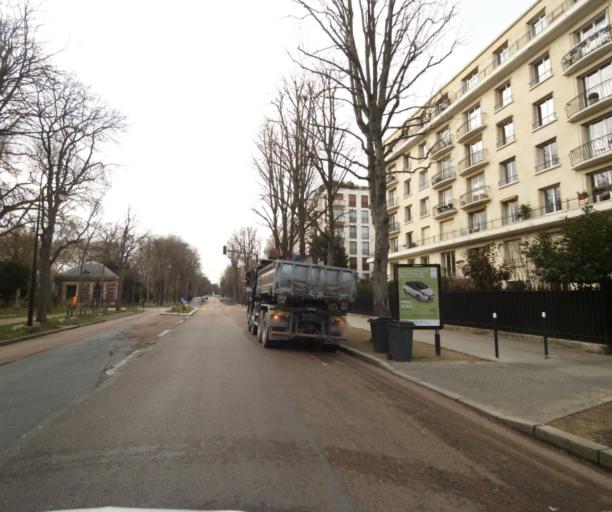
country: FR
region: Ile-de-France
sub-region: Departement des Hauts-de-Seine
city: Neuilly-sur-Seine
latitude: 48.8772
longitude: 2.2567
